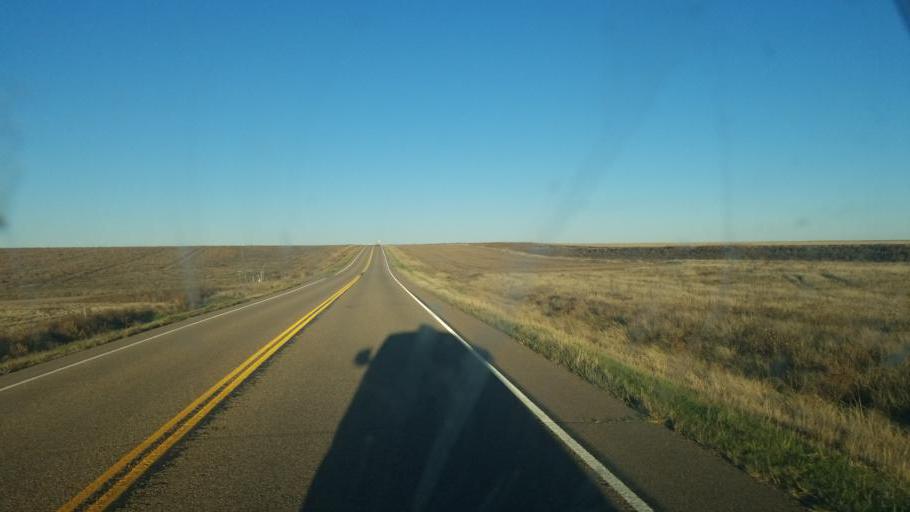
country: US
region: Colorado
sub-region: Cheyenne County
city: Cheyenne Wells
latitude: 38.8150
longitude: -102.4804
